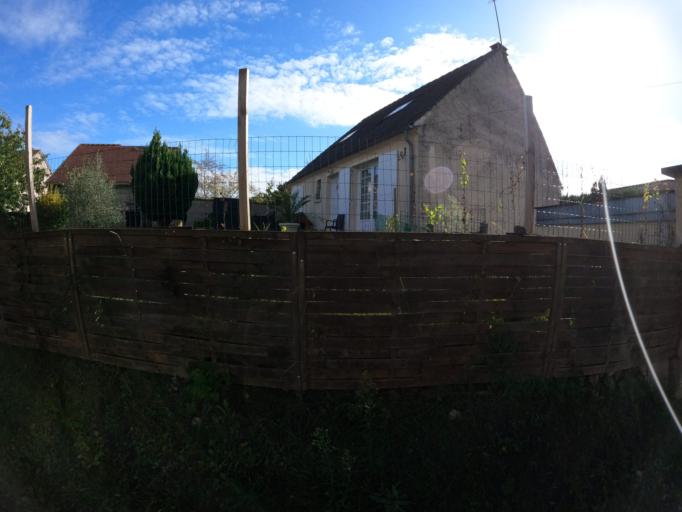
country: FR
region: Ile-de-France
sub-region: Departement de Seine-et-Marne
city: Montry
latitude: 48.8853
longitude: 2.8275
